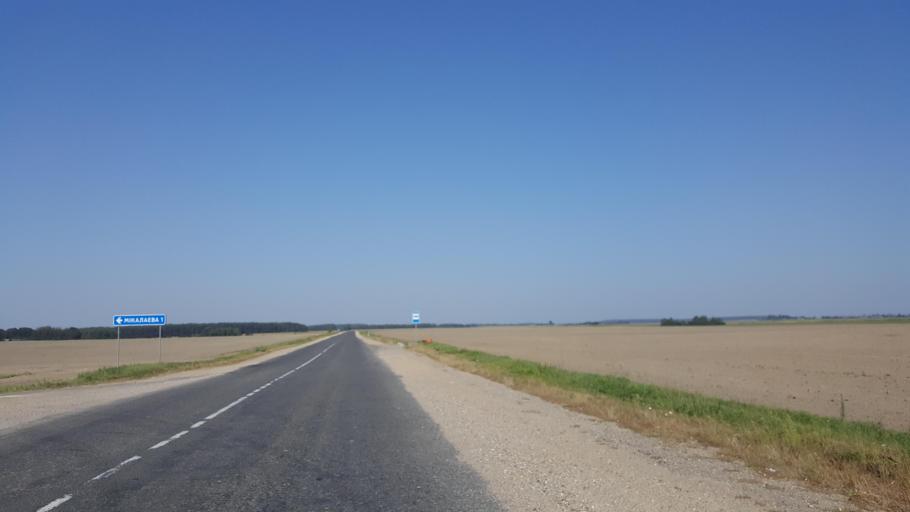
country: BY
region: Brest
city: Kamyanyets
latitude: 52.4028
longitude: 23.7663
